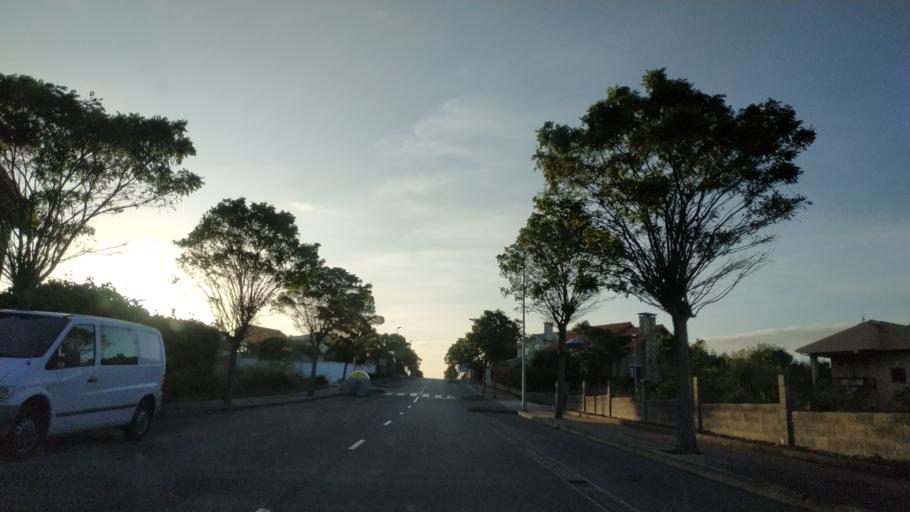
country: ES
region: Galicia
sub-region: Provincia da Coruna
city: Oleiros
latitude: 43.3704
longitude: -8.3396
